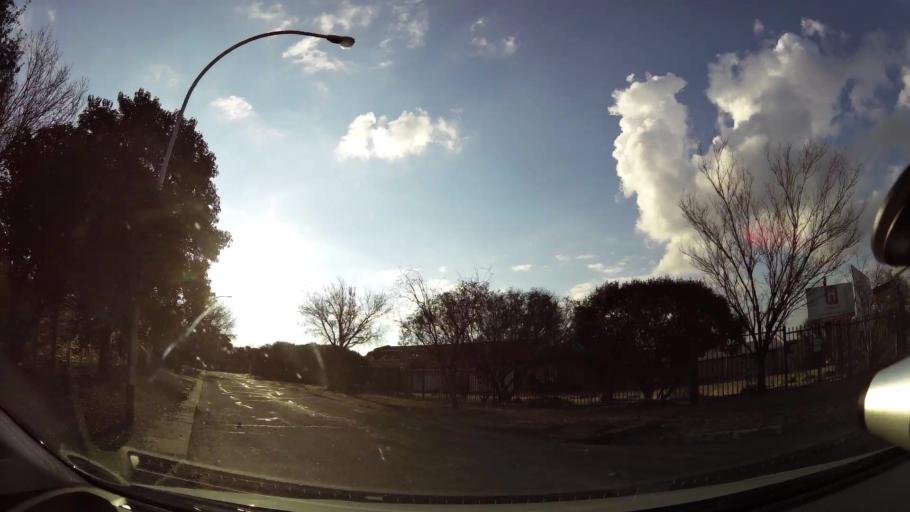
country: ZA
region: Orange Free State
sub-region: Mangaung Metropolitan Municipality
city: Bloemfontein
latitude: -29.1511
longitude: 26.1852
